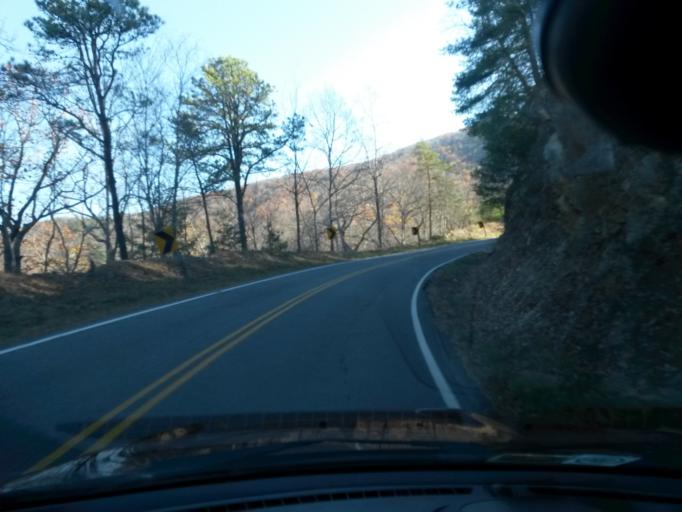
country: US
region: Virginia
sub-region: Botetourt County
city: Buchanan
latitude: 37.5084
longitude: -79.6638
